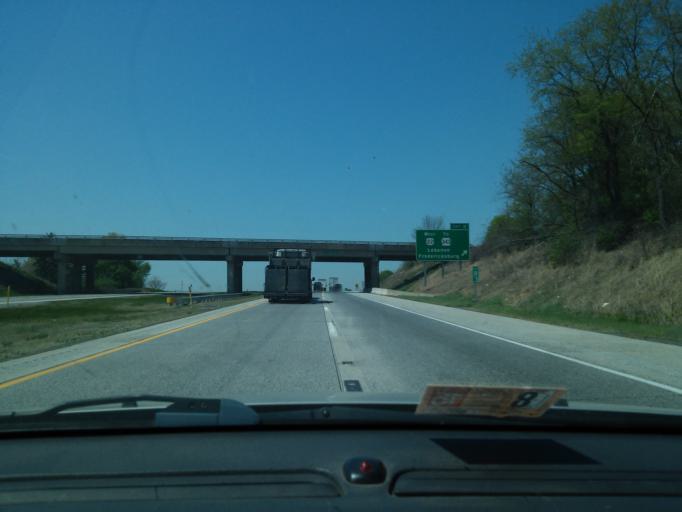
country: US
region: Pennsylvania
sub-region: Lebanon County
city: Fredericksburg
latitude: 40.4565
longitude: -76.3776
